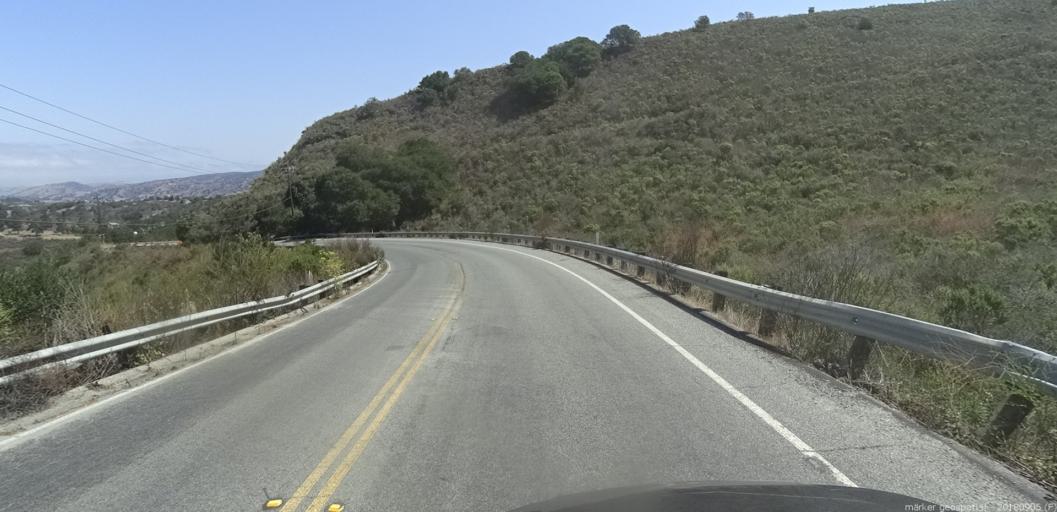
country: US
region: California
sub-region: Monterey County
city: Carmel Valley Village
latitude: 36.5553
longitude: -121.7557
